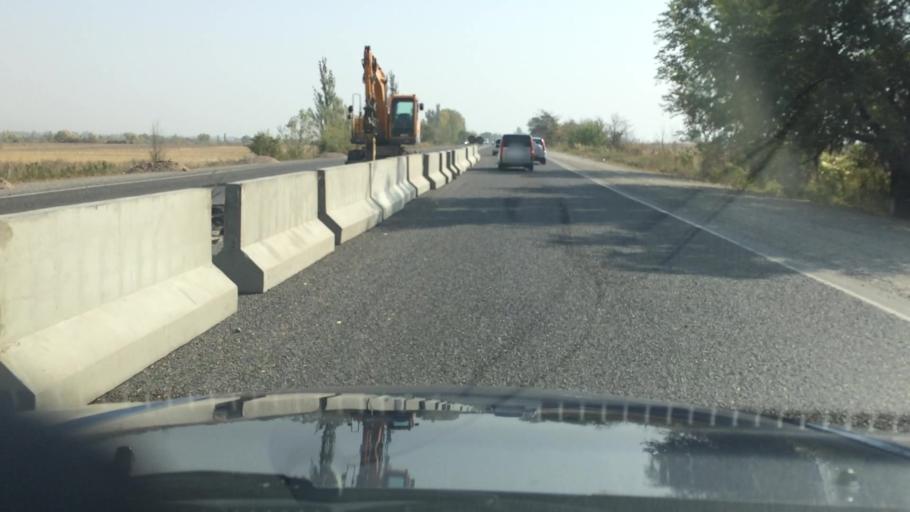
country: KG
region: Chuy
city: Kant
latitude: 42.9577
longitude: 74.9289
